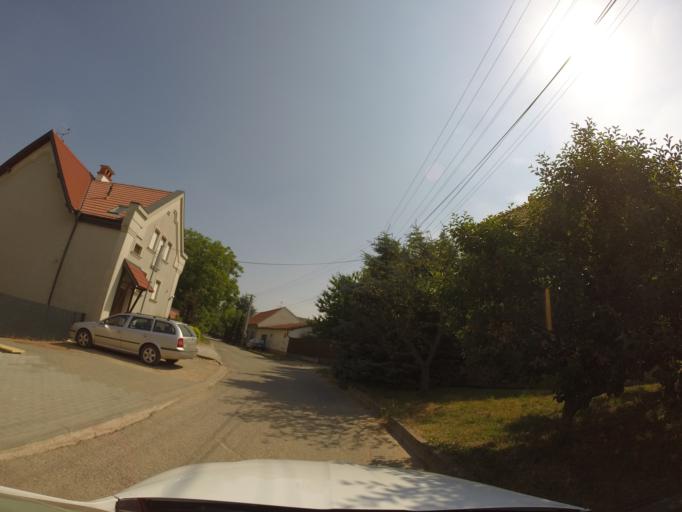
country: CZ
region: South Moravian
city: Sakvice
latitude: 48.8707
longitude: 16.6659
